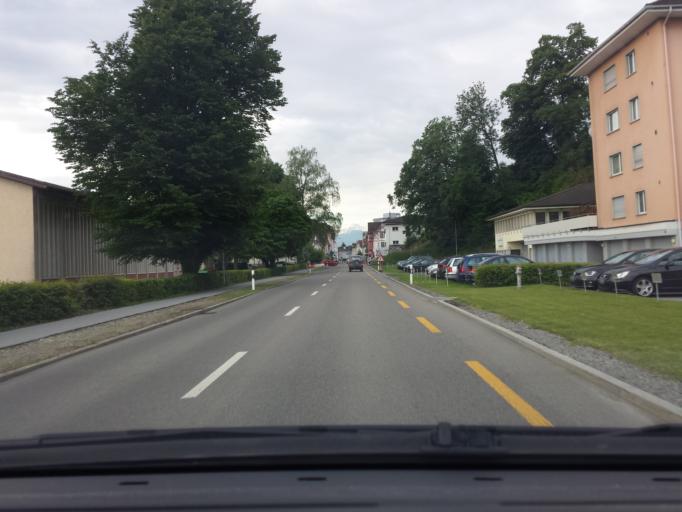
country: CH
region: Appenzell Innerrhoden
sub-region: Appenzell Inner Rhodes
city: Balgach
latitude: 47.4139
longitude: 9.6250
